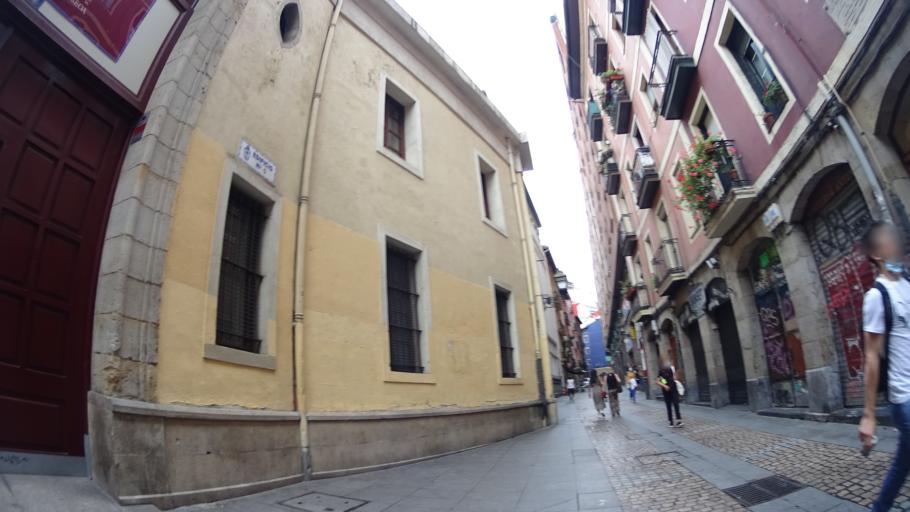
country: ES
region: Basque Country
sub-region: Bizkaia
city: Santutxu
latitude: 43.2581
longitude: -2.9204
